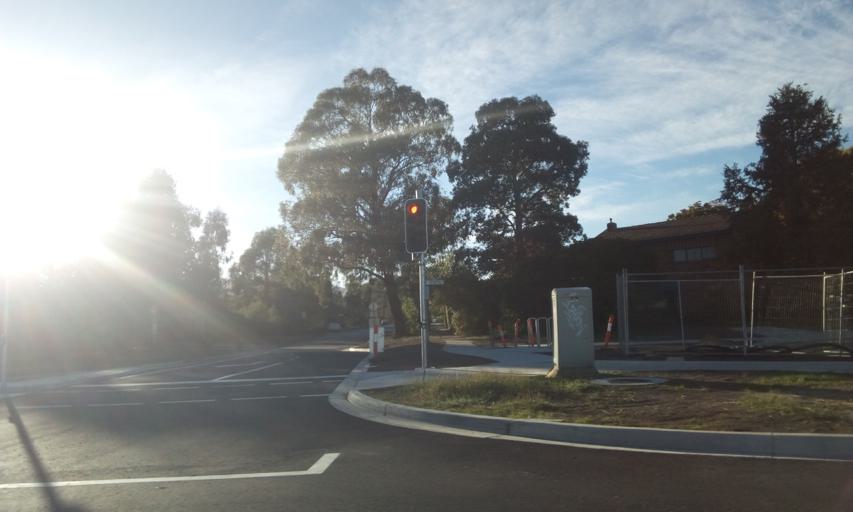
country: AU
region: Australian Capital Territory
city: Acton
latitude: -35.2440
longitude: 149.1346
